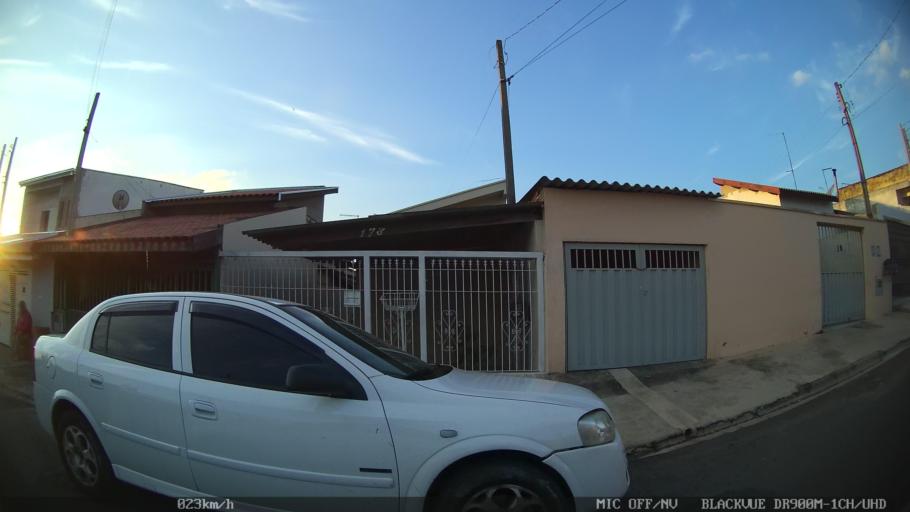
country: BR
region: Sao Paulo
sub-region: Hortolandia
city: Hortolandia
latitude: -22.8600
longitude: -47.2059
